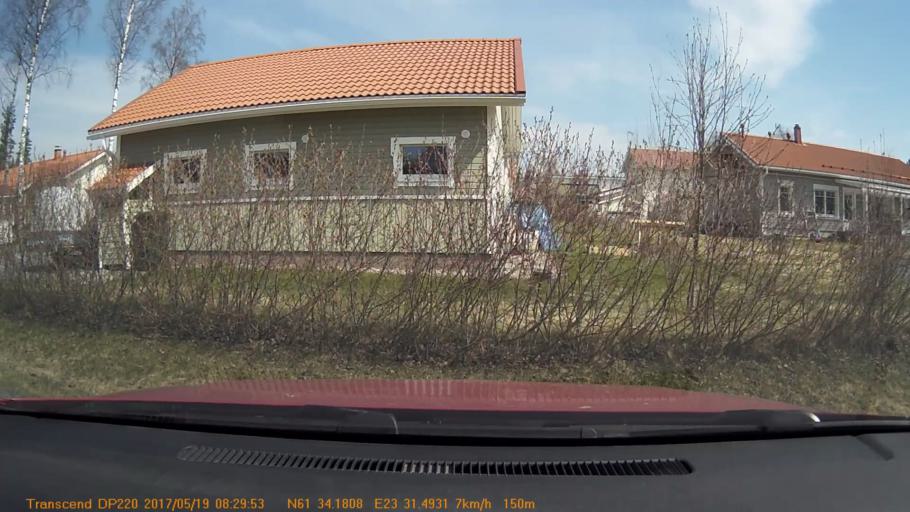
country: FI
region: Pirkanmaa
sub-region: Tampere
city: Yloejaervi
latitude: 61.5697
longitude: 23.5249
